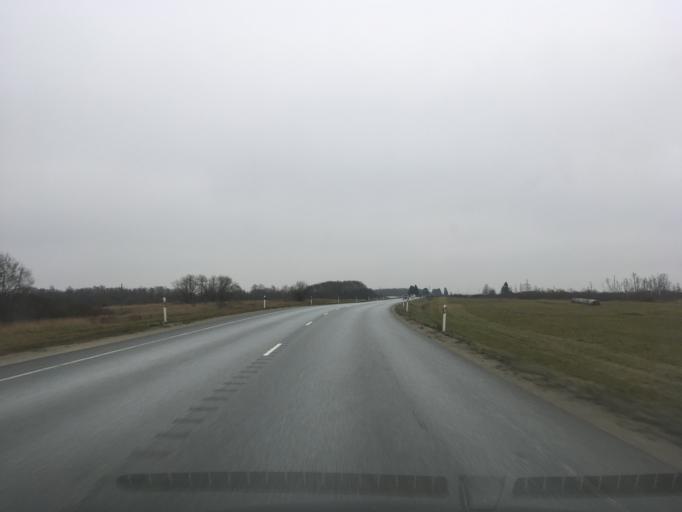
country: EE
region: Ida-Virumaa
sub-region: Kivioli linn
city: Kivioli
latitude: 59.4258
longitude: 26.9604
